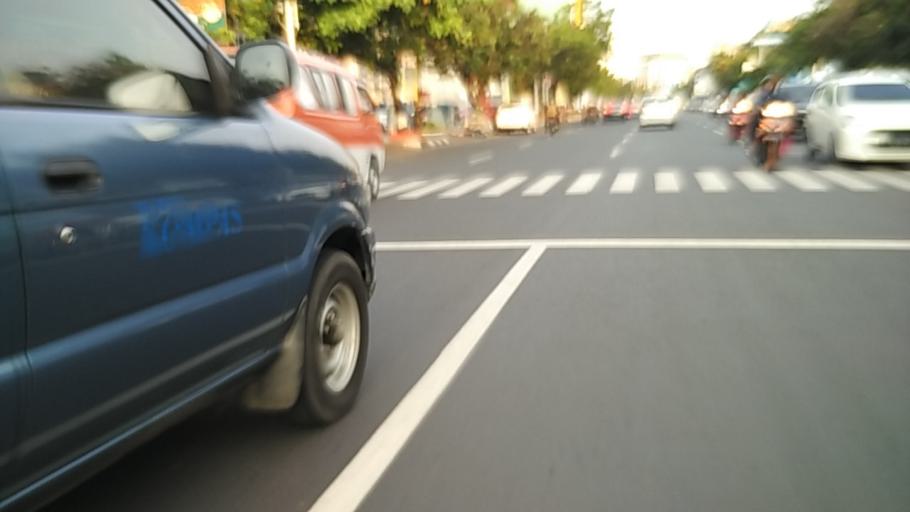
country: ID
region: Central Java
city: Semarang
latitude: -6.9869
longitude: 110.4153
